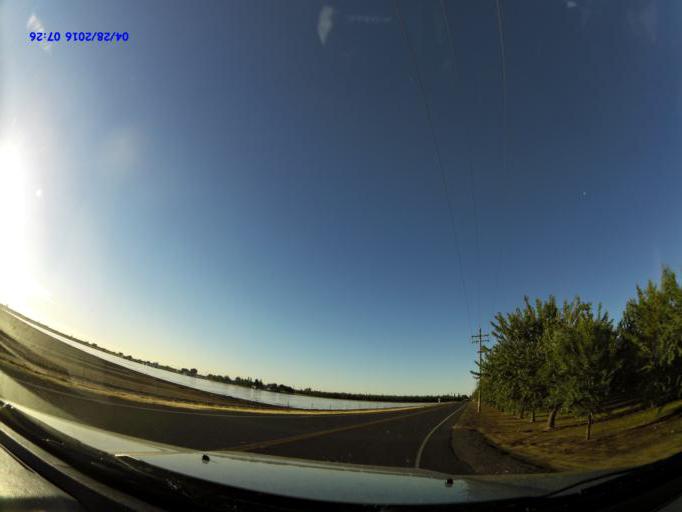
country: US
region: California
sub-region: San Joaquin County
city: Manteca
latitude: 37.8262
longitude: -121.1810
